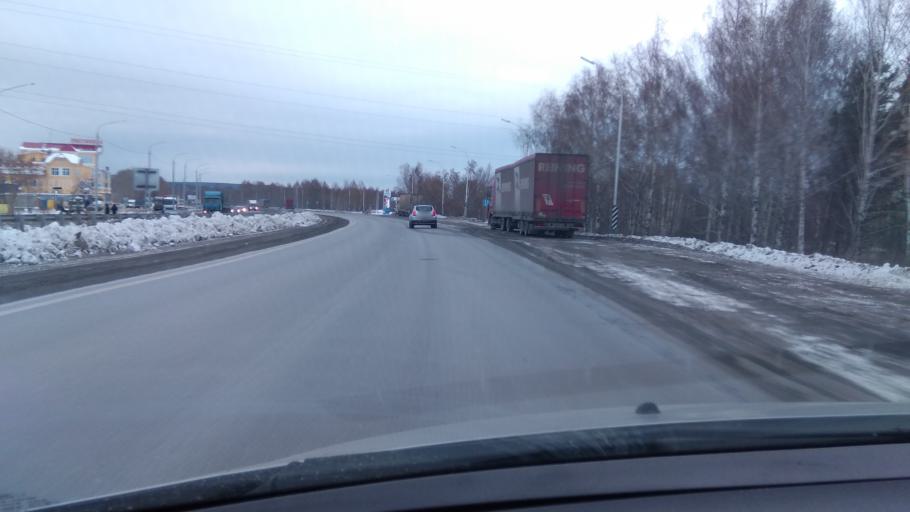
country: RU
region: Sverdlovsk
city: Aramil
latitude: 56.7040
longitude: 60.7476
